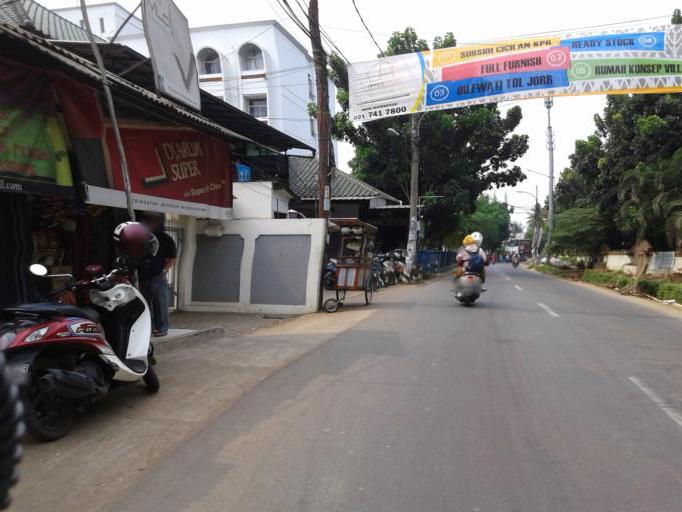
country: ID
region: West Java
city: Pamulang
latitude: -6.3098
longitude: 106.7588
